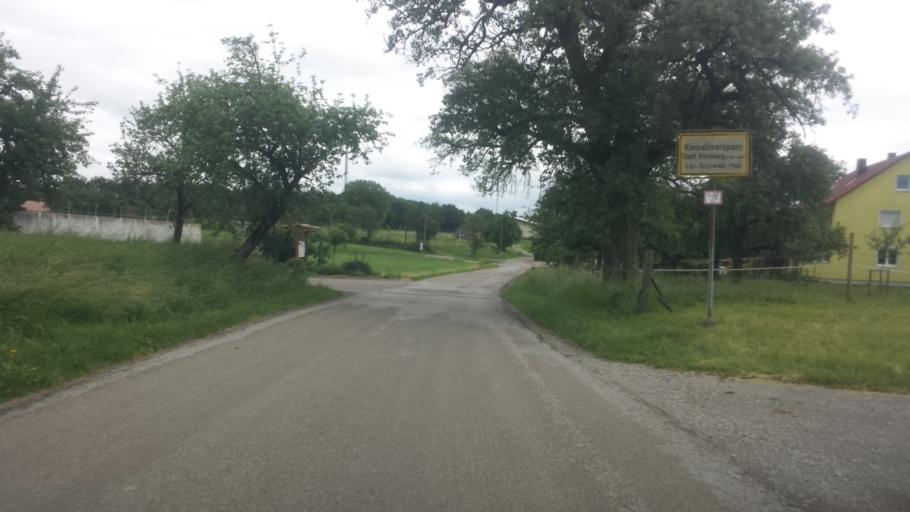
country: DE
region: Baden-Wuerttemberg
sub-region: Regierungsbezirk Stuttgart
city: Ilshofen
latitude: 49.1745
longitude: 9.9516
